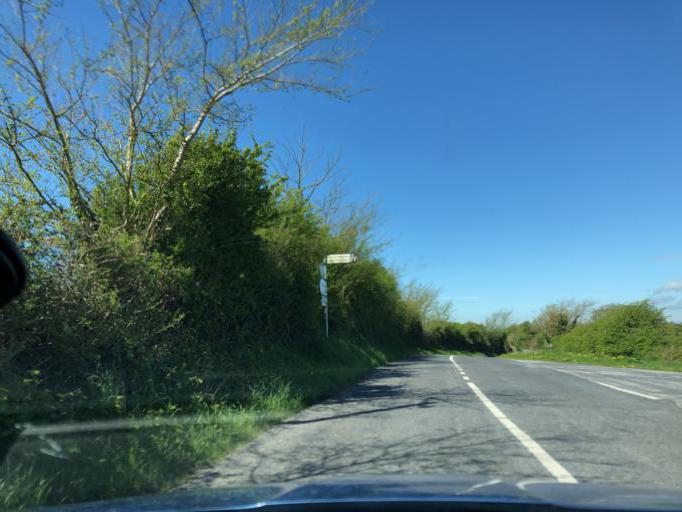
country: IE
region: Connaught
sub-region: County Galway
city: Loughrea
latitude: 53.1576
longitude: -8.3896
